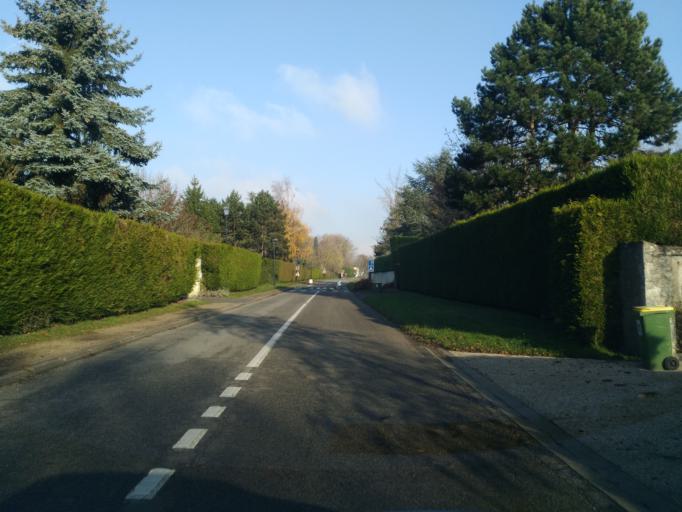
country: FR
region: Ile-de-France
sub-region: Departement des Yvelines
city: Feucherolles
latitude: 48.8800
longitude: 1.9806
